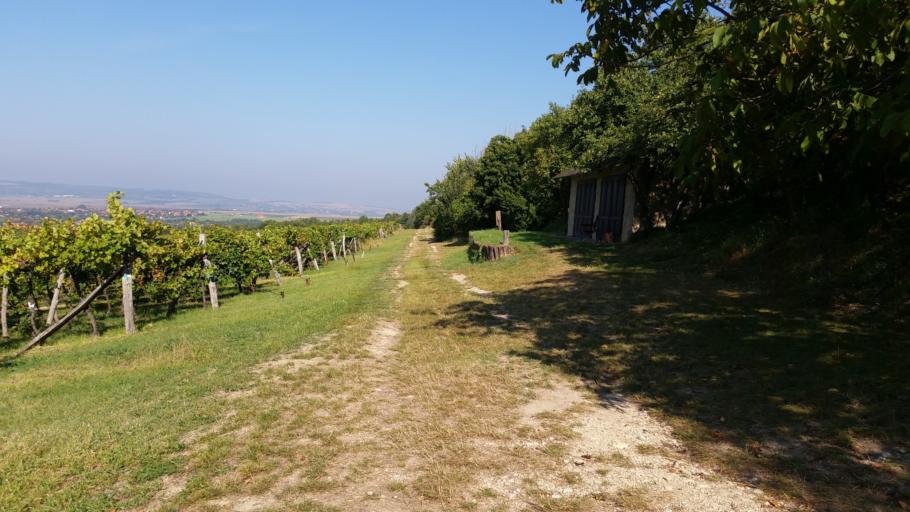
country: HU
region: Pest
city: Telki
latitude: 47.5483
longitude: 18.8379
